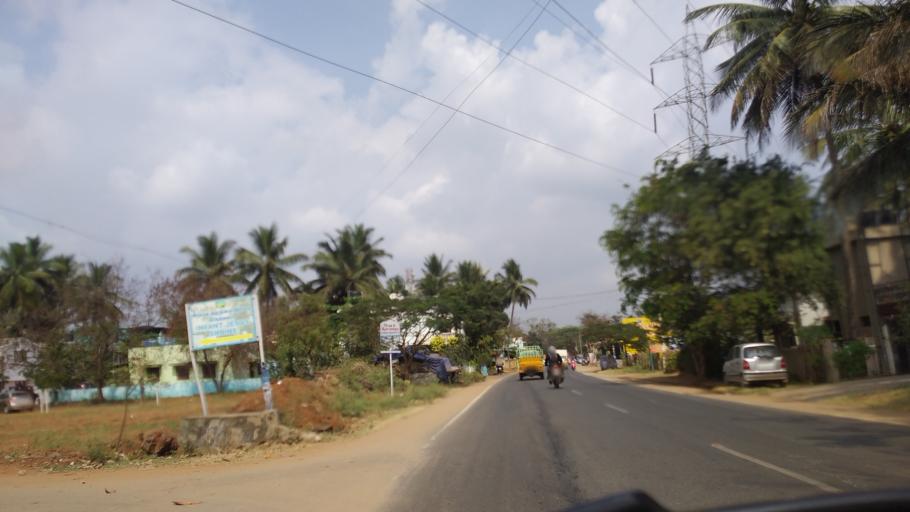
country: IN
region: Tamil Nadu
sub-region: Coimbatore
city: Perur
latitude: 10.9474
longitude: 76.9361
